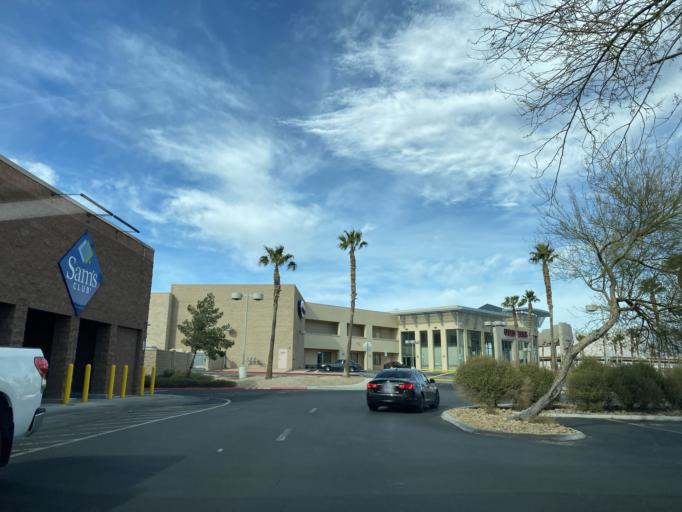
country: US
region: Nevada
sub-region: Clark County
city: Las Vegas
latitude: 36.2735
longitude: -115.2704
